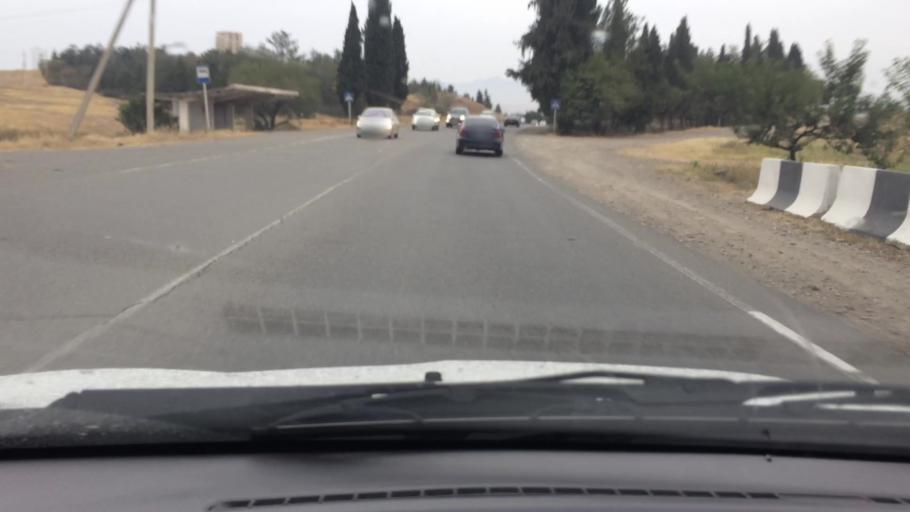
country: GE
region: Kvemo Kartli
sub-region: Marneuli
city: Marneuli
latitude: 41.5218
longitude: 44.7792
